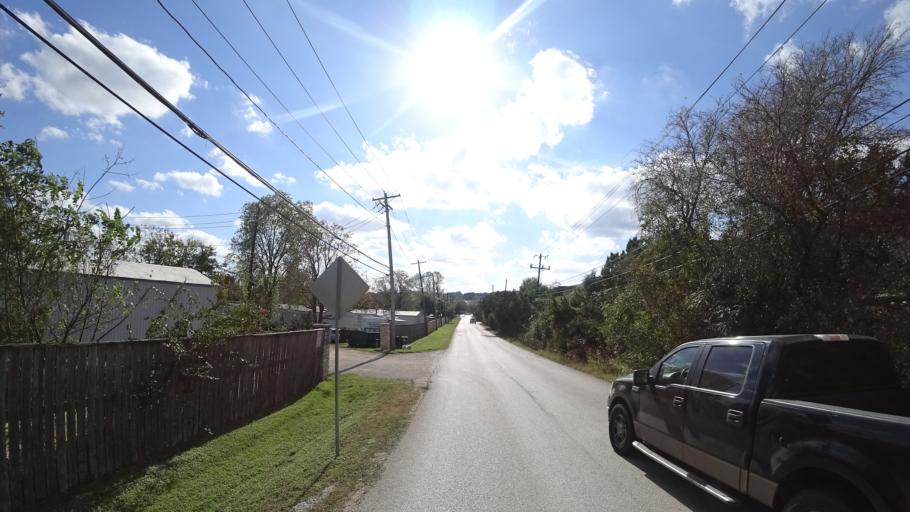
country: US
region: Texas
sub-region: Travis County
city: Barton Creek
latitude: 30.2495
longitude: -97.8870
